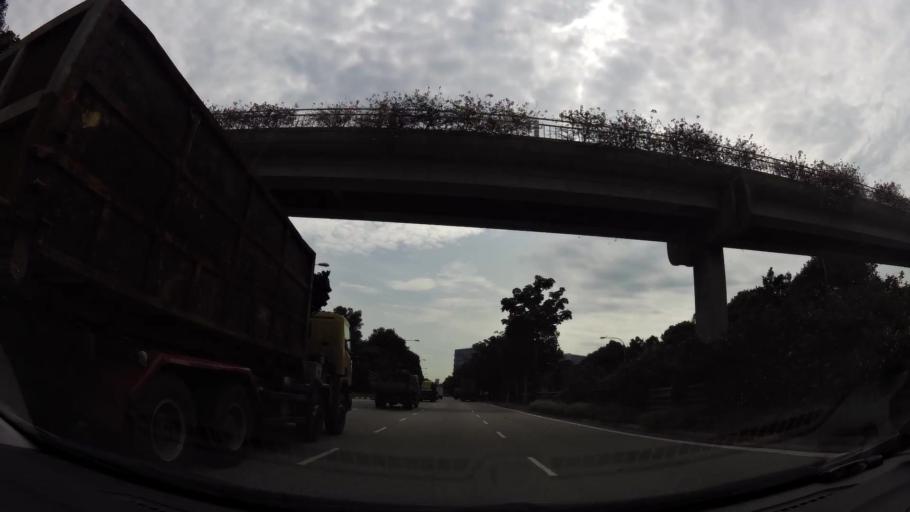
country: SG
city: Singapore
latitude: 1.3146
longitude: 103.6984
